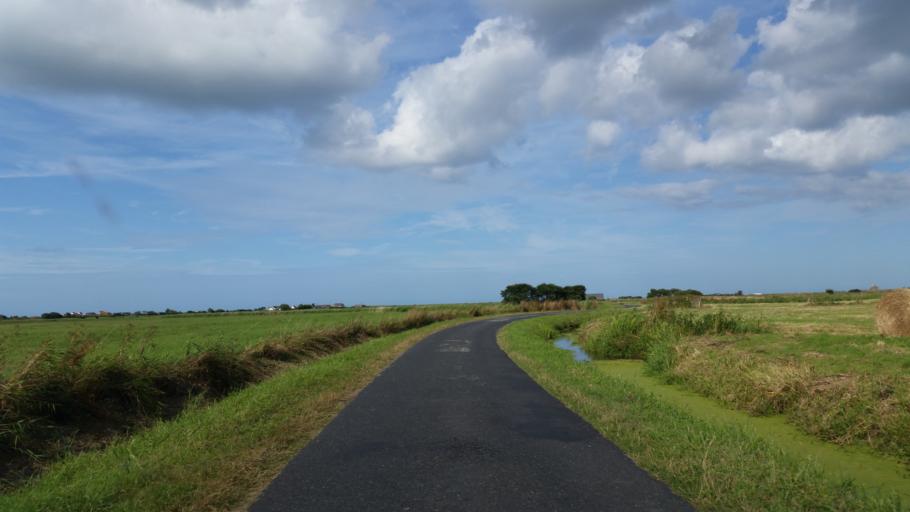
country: FR
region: Lower Normandy
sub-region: Departement de la Manche
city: Sainte-Mere-Eglise
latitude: 49.4536
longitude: -1.2401
